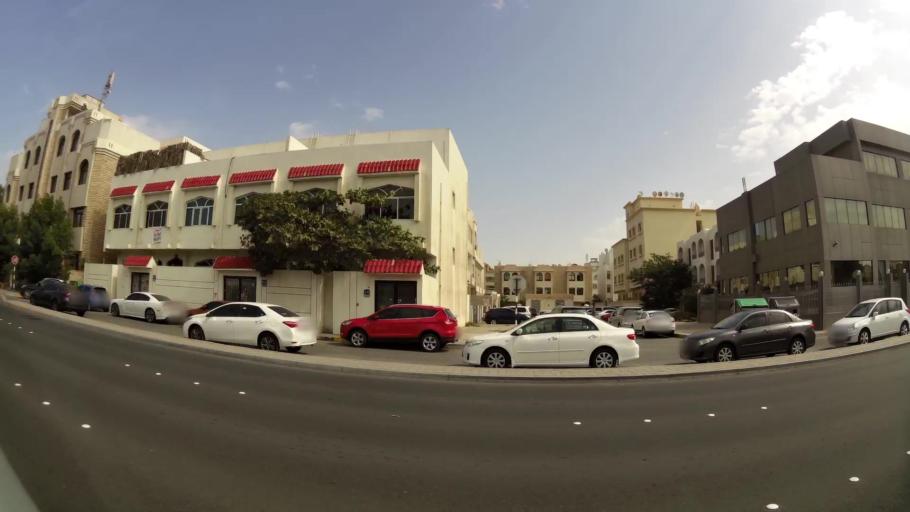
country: AE
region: Abu Dhabi
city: Abu Dhabi
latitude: 24.4558
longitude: 54.3564
